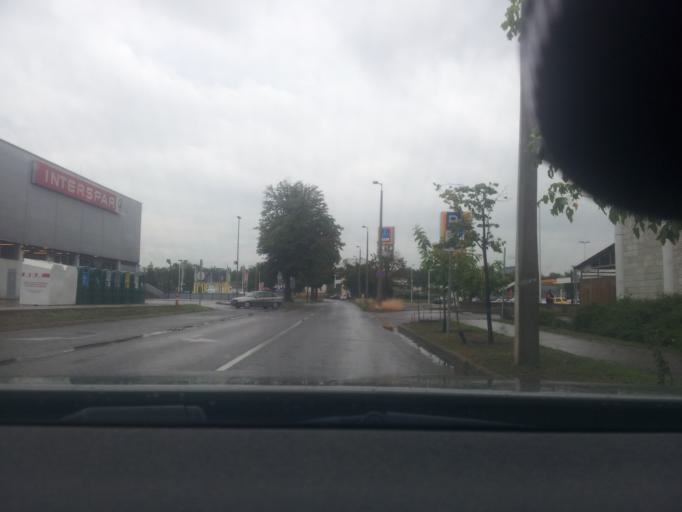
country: HU
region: Budapest
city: Budapest XIX. keruelet
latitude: 47.4619
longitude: 19.1300
